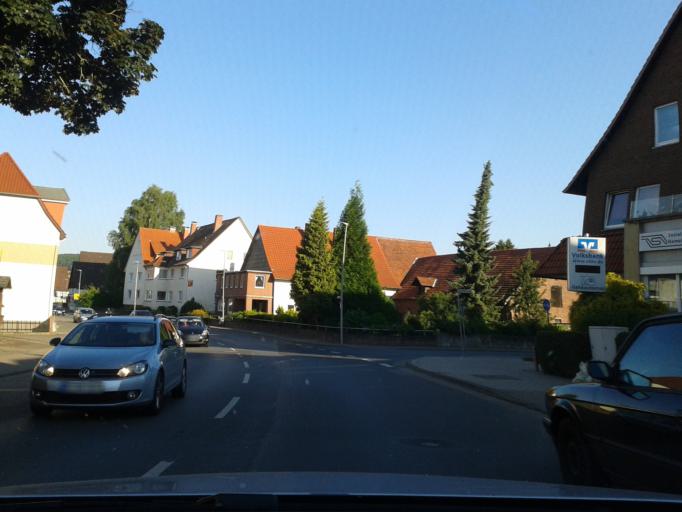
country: DE
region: Lower Saxony
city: Bad Pyrmont
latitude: 51.9857
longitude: 9.2388
